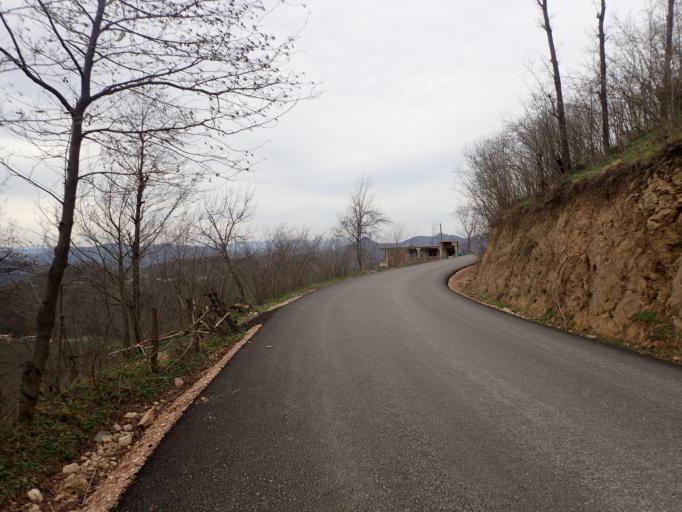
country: TR
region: Ordu
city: Camas
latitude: 40.8861
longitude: 37.5149
